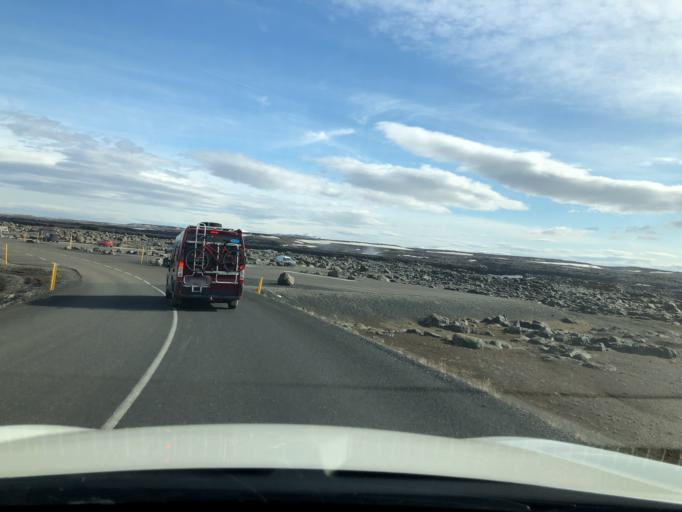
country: IS
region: Northeast
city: Husavik
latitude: 65.8107
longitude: -16.4013
